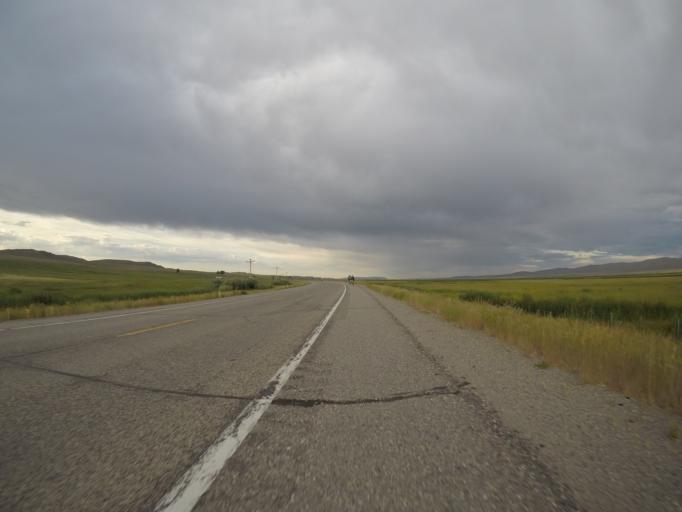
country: US
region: Utah
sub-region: Rich County
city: Randolph
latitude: 42.0156
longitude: -110.9369
